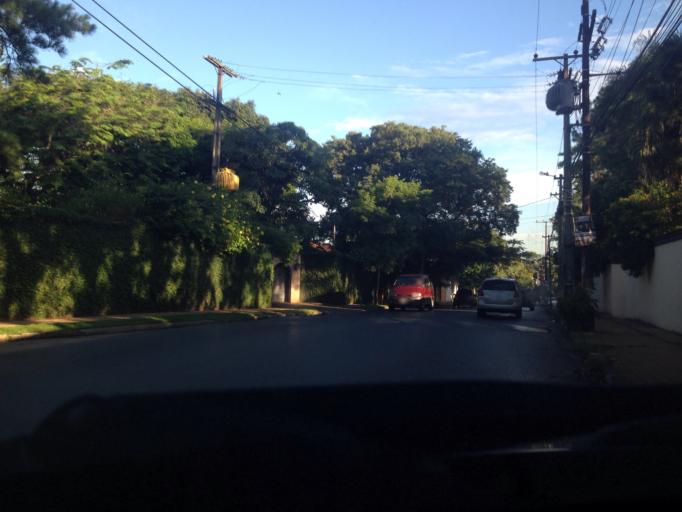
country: PY
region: Central
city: Lambare
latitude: -25.3220
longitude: -57.5851
